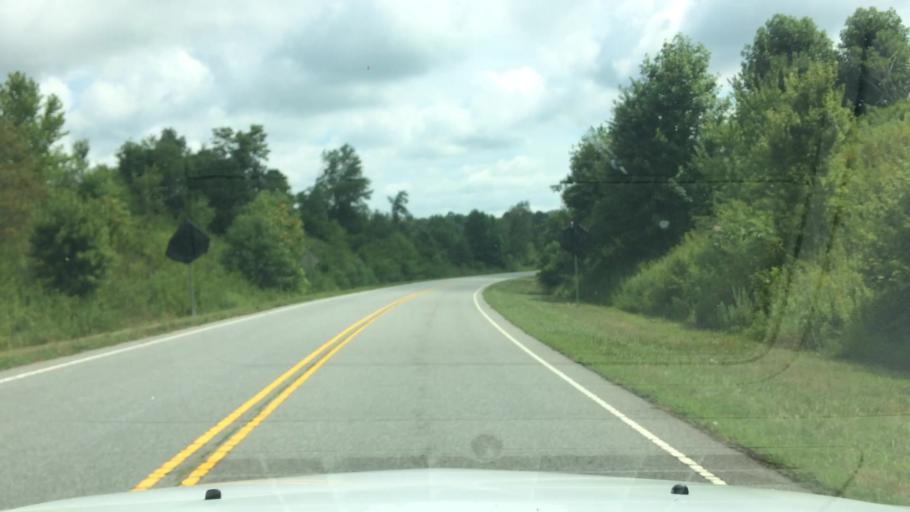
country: US
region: North Carolina
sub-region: Yadkin County
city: Jonesville
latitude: 36.1203
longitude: -80.8553
